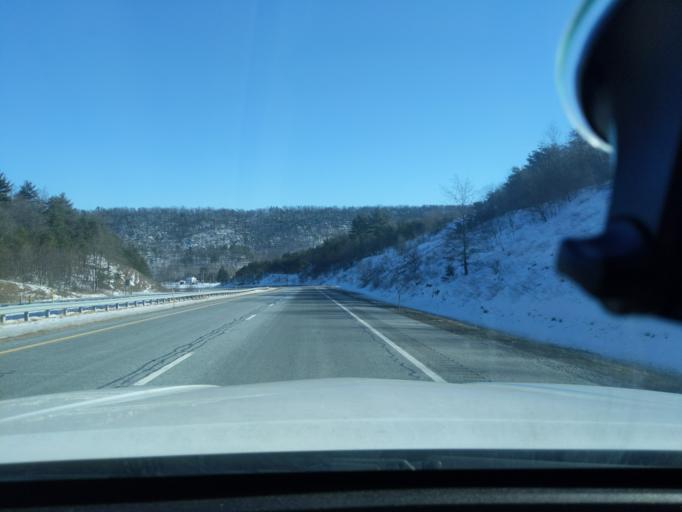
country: US
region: Maryland
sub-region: Washington County
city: Hancock
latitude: 39.7007
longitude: -78.2535
